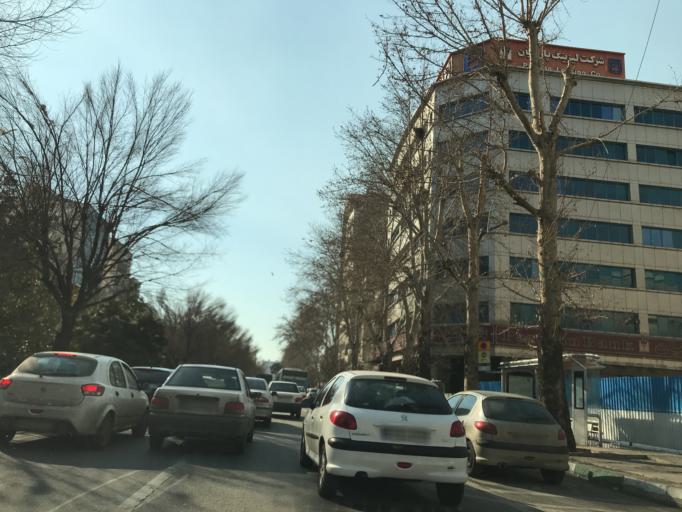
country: IR
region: Tehran
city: Tehran
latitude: 35.7102
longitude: 51.4014
